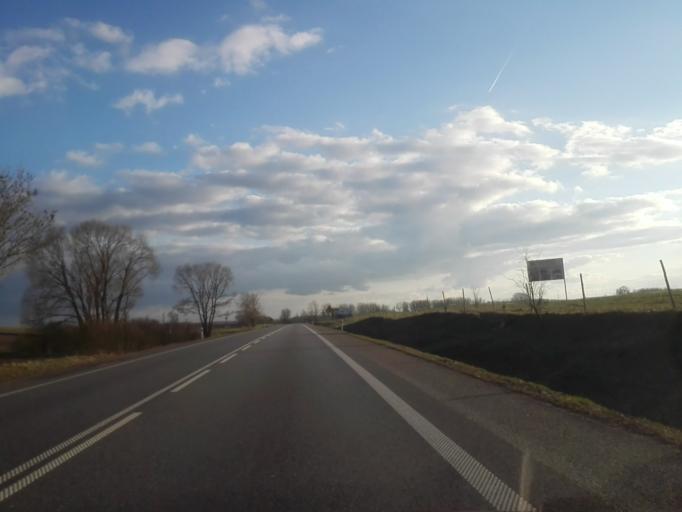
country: PL
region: Podlasie
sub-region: Suwalki
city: Suwalki
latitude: 54.2024
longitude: 23.0219
